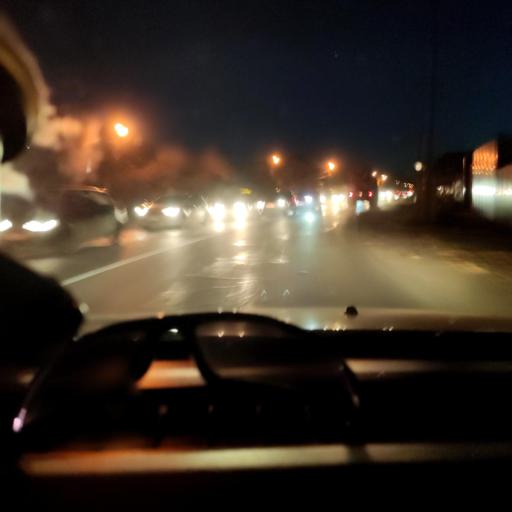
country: RU
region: Samara
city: Rozhdestveno
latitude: 53.1503
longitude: 50.0697
